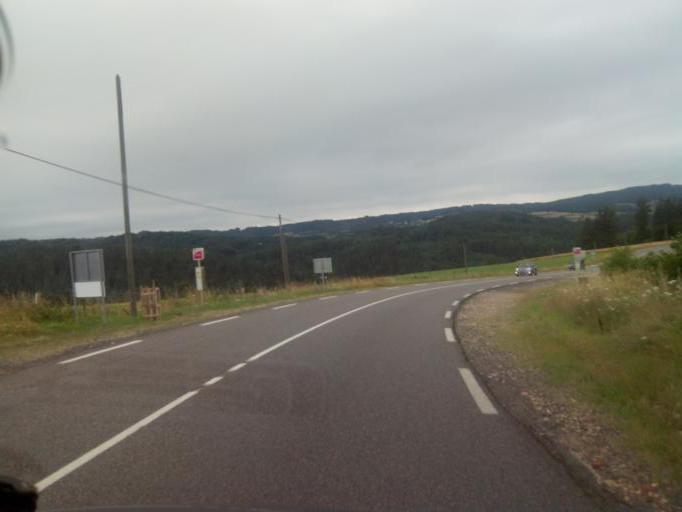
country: FR
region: Rhone-Alpes
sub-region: Departement de la Loire
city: Usson-en-Forez
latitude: 45.3555
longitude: 3.9031
